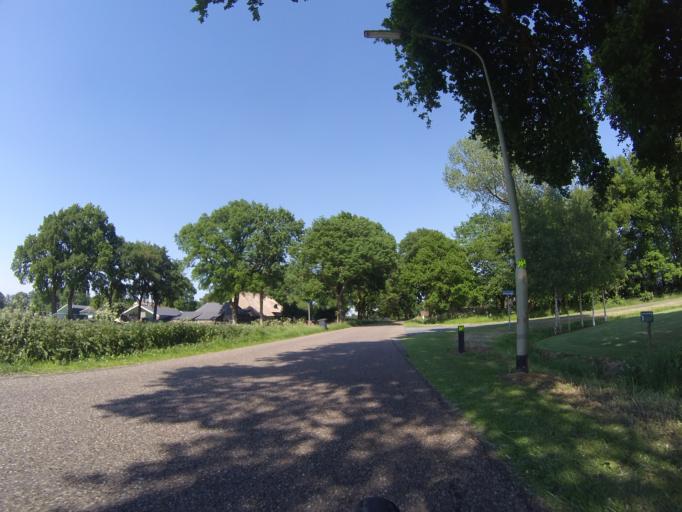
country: NL
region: Drenthe
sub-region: Gemeente Coevorden
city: Sleen
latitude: 52.7425
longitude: 6.8198
